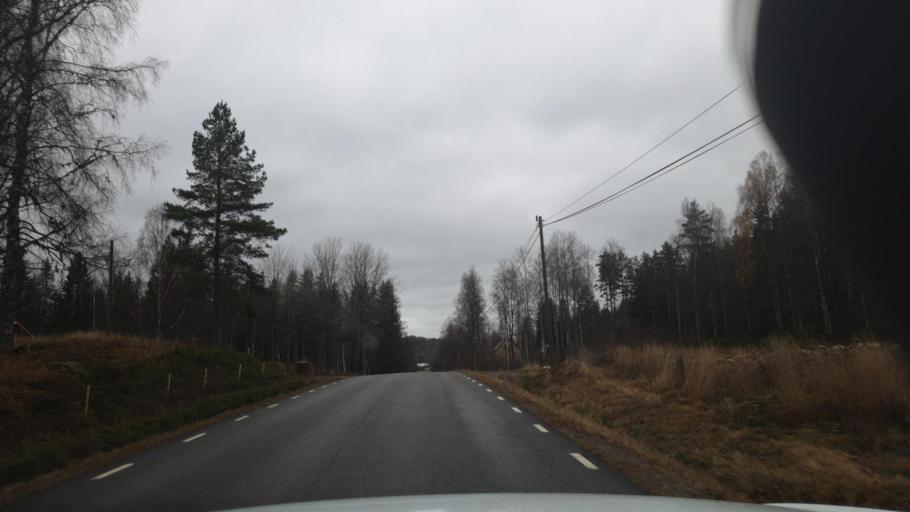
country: SE
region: Vaermland
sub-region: Eda Kommun
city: Amotfors
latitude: 59.9229
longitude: 12.5209
